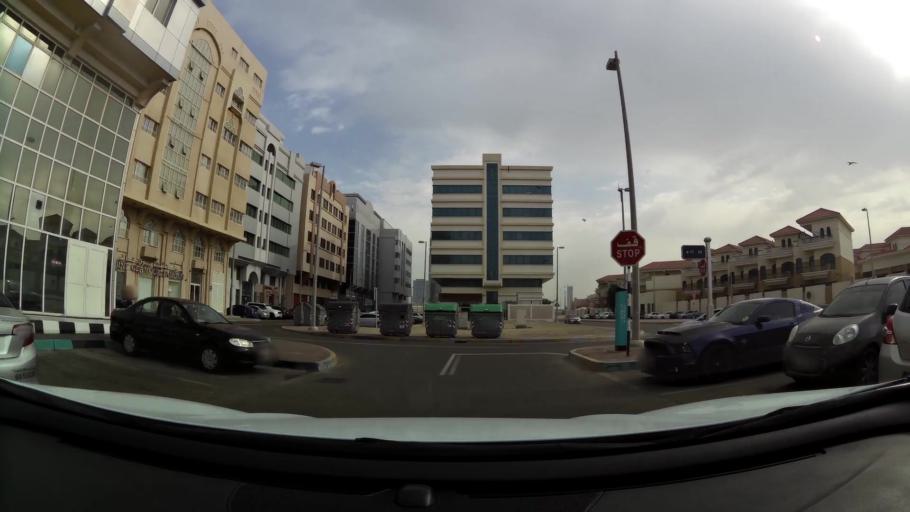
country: AE
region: Abu Dhabi
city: Abu Dhabi
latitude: 24.4775
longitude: 54.3832
